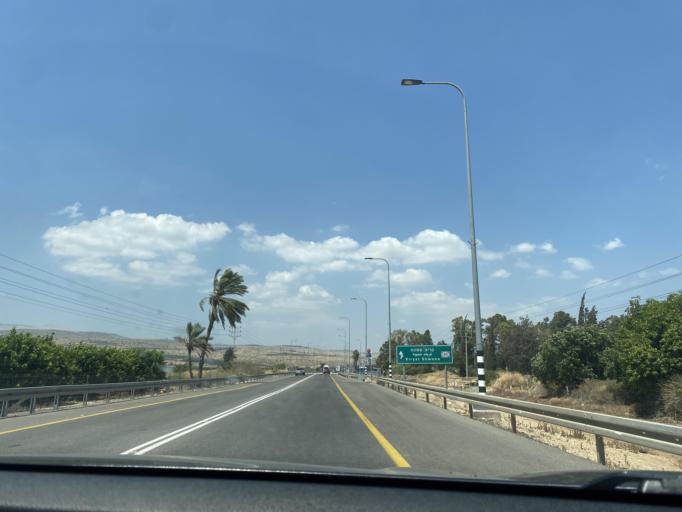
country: IL
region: Northern District
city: Tiberias
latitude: 32.8428
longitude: 35.5144
